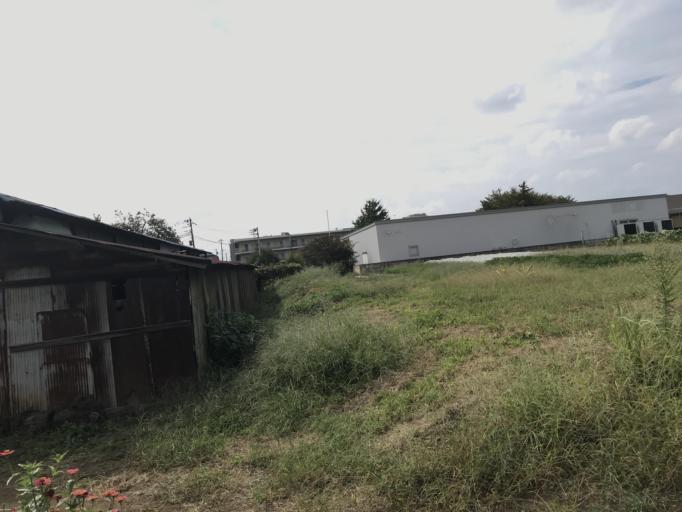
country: JP
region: Tokyo
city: Tanashicho
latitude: 35.7757
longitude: 139.5412
